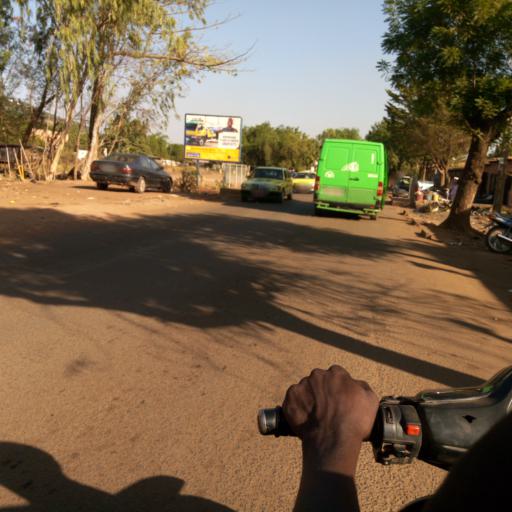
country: ML
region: Bamako
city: Bamako
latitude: 12.6546
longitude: -8.0223
